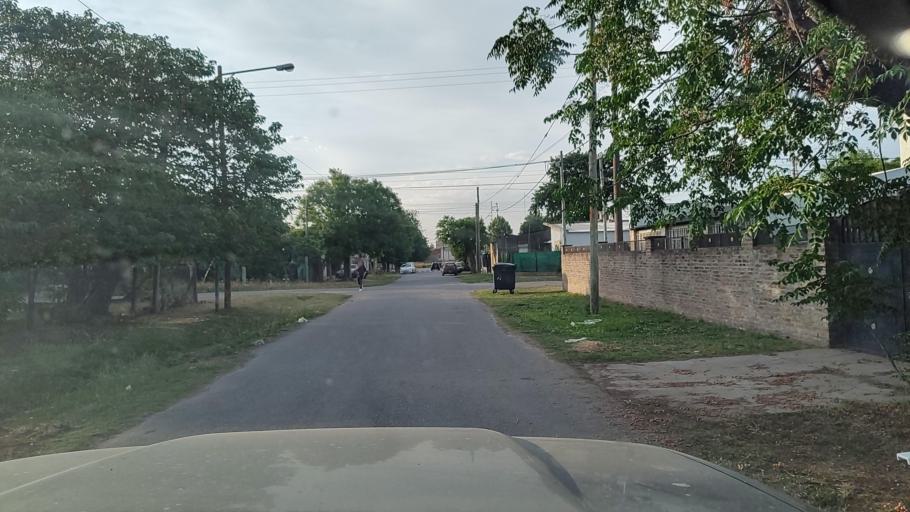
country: AR
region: Buenos Aires
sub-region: Partido de Lujan
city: Lujan
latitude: -34.5688
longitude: -59.1358
